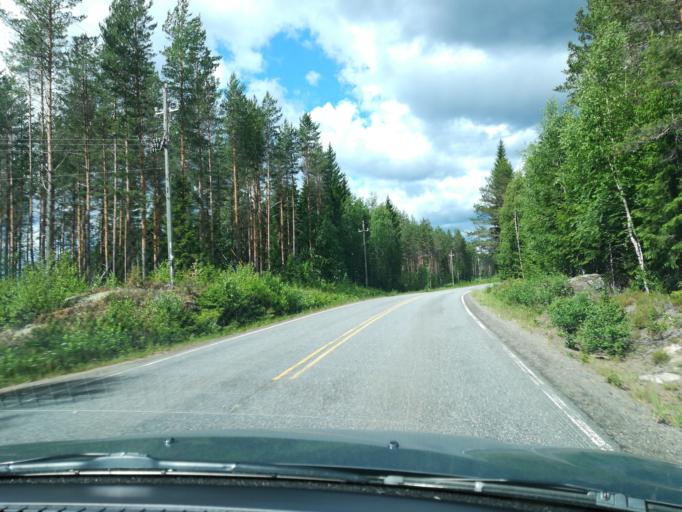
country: FI
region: Southern Savonia
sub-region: Mikkeli
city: Ristiina
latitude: 61.3482
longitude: 27.1518
